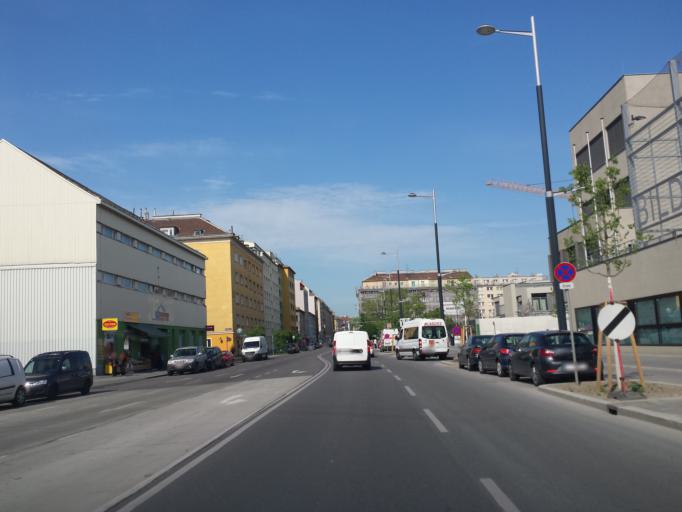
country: AT
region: Vienna
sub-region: Wien Stadt
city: Vienna
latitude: 48.1777
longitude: 16.3830
